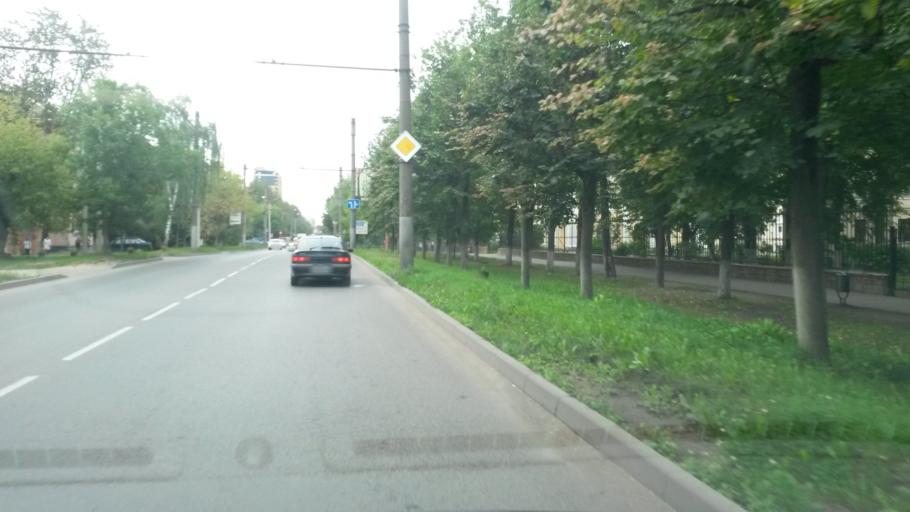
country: RU
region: Ivanovo
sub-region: Gorod Ivanovo
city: Ivanovo
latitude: 57.0197
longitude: 40.9564
